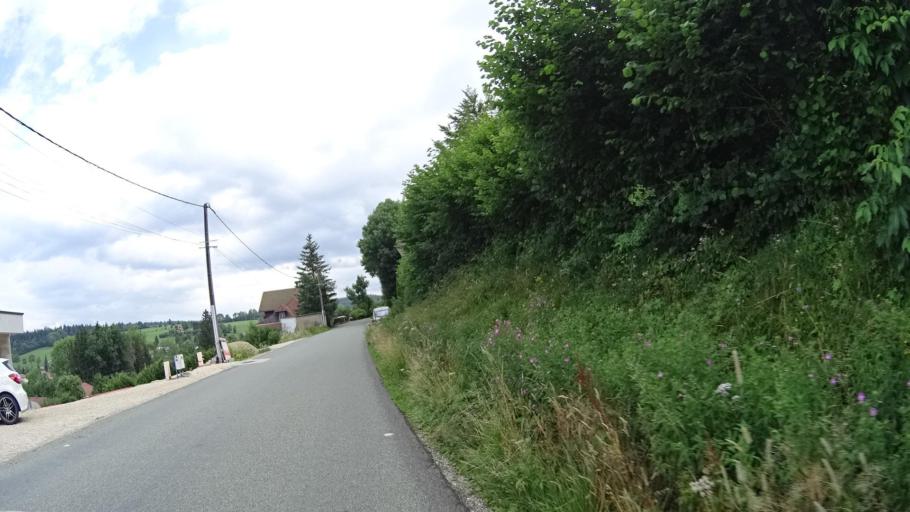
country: FR
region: Franche-Comte
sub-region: Departement du Doubs
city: Les Fourgs
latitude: 46.8317
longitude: 6.3415
